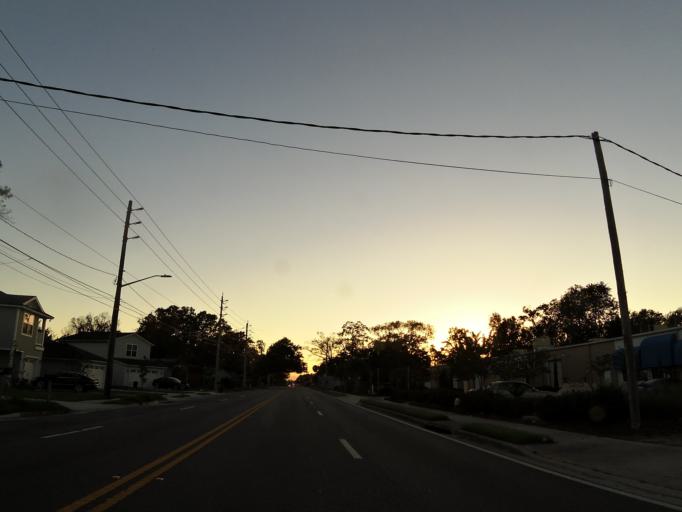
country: US
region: Florida
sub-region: Duval County
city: Jacksonville
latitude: 30.3177
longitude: -81.7255
